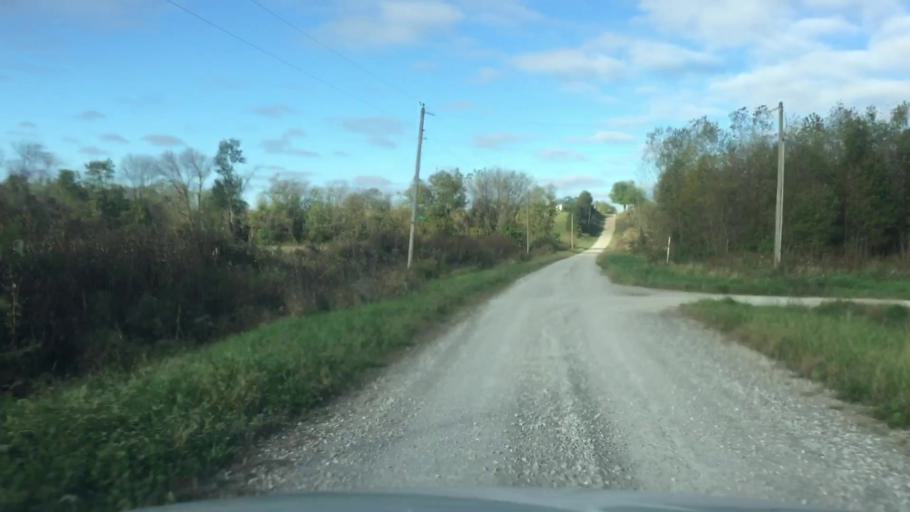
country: US
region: Missouri
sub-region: Howard County
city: New Franklin
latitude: 39.0833
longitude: -92.7690
